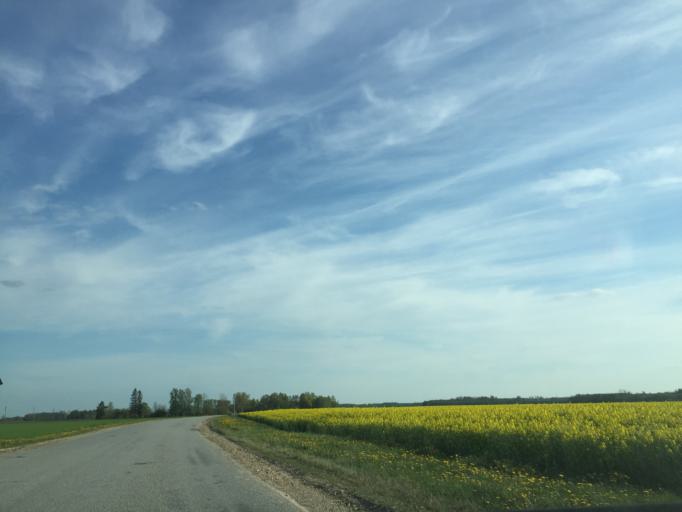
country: LV
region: Bauskas Rajons
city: Bauska
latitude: 56.3632
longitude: 24.2306
